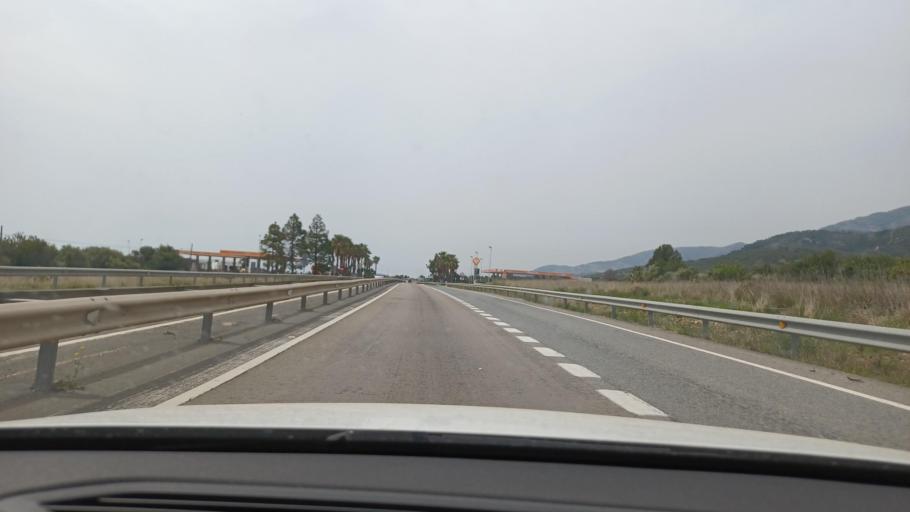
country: ES
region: Catalonia
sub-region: Provincia de Tarragona
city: Sant Carles de la Rapita
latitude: 40.6279
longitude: 0.5800
